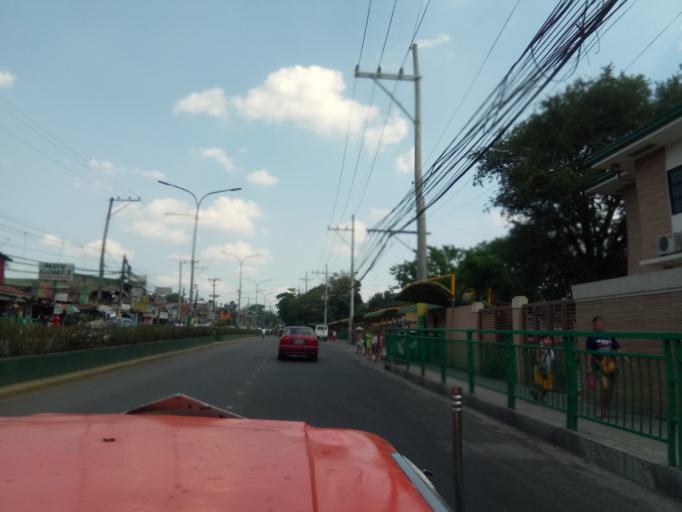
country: PH
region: Calabarzon
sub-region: Province of Cavite
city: Dasmarinas
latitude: 14.3274
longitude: 120.9599
